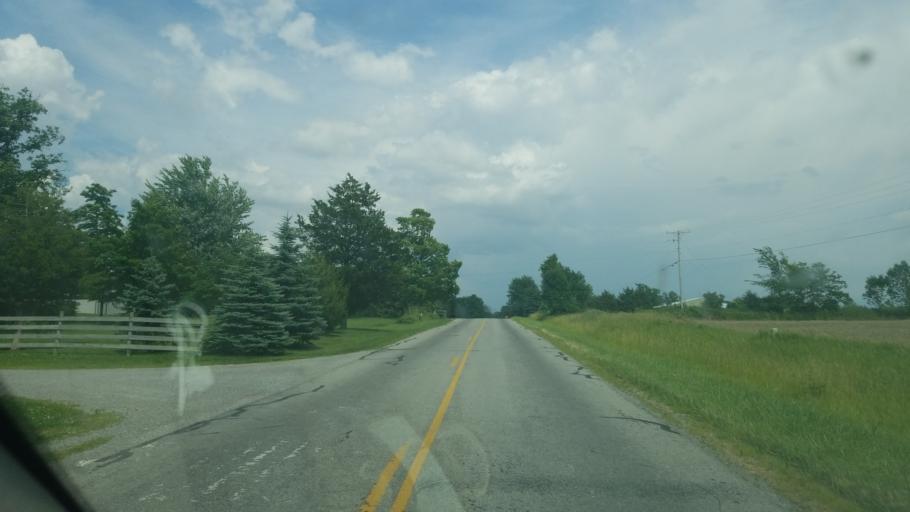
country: US
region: Ohio
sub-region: Logan County
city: Northwood
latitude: 40.4646
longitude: -83.7218
